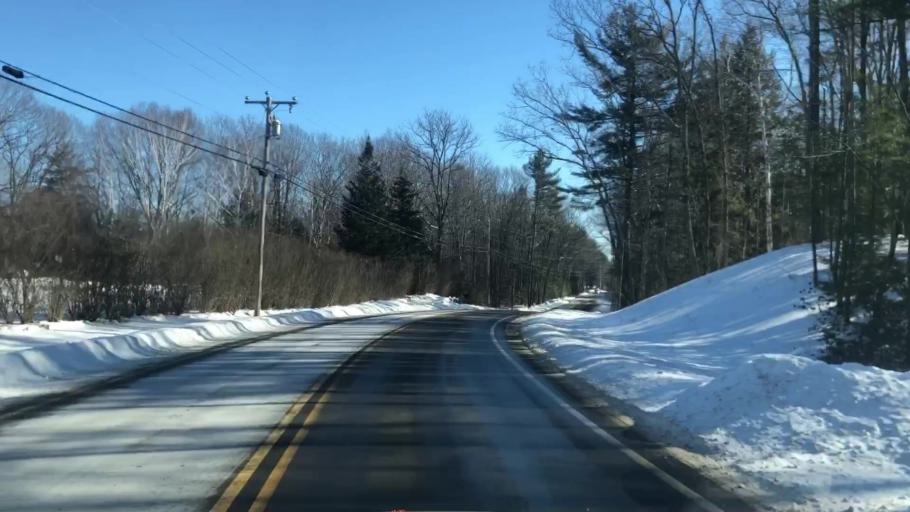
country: US
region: New Hampshire
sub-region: Hillsborough County
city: Bedford
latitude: 42.9448
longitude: -71.5482
